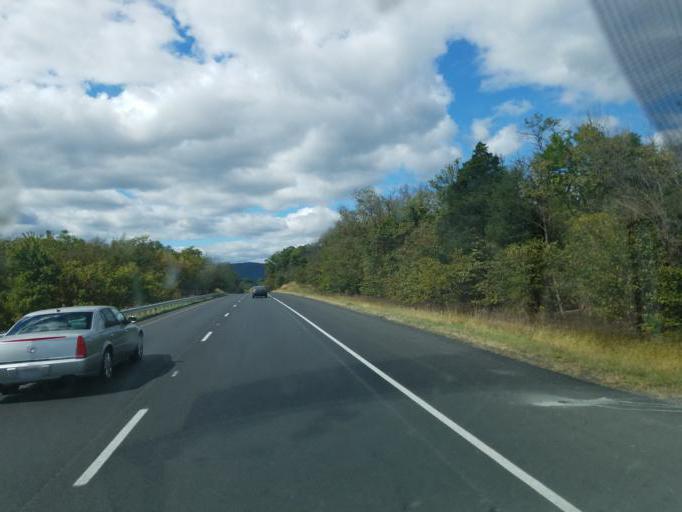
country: US
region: Maryland
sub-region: Washington County
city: Wilson-Conococheague
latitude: 39.6520
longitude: -77.8887
